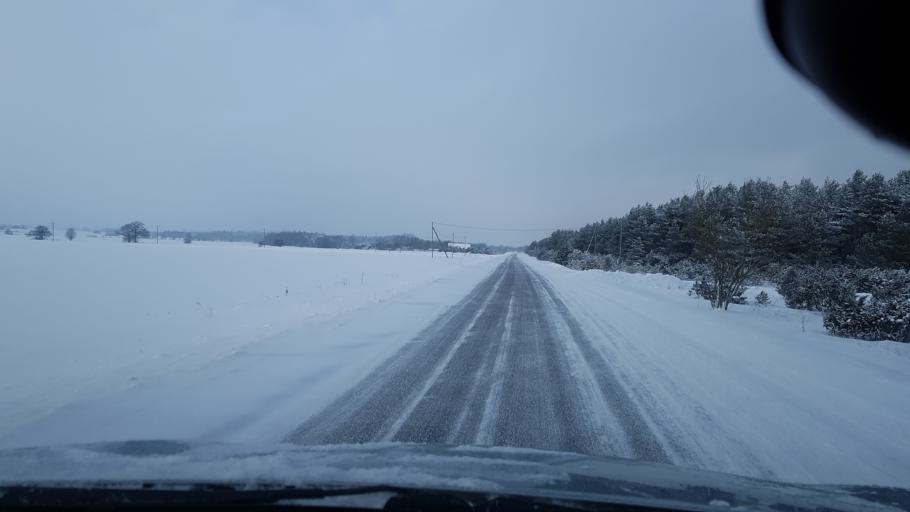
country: EE
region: Harju
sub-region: Keila linn
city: Keila
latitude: 59.3562
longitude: 24.4247
